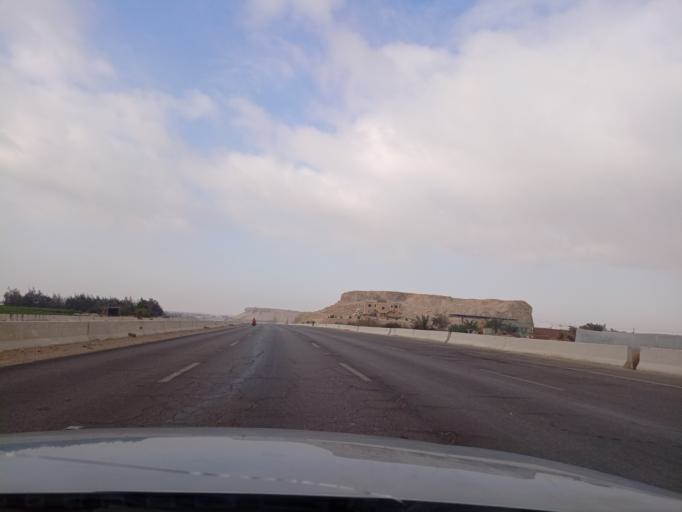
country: EG
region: Al Jizah
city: Al `Ayyat
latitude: 29.6801
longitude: 31.2141
